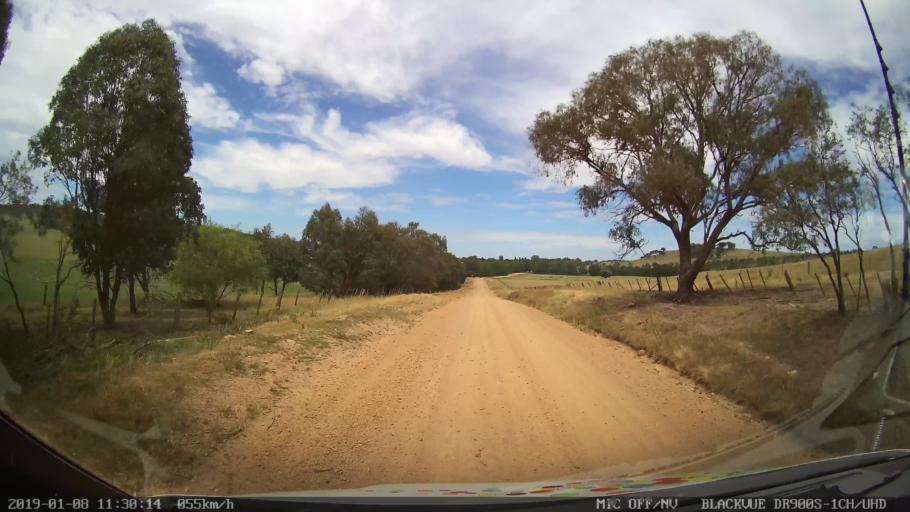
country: AU
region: New South Wales
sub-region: Guyra
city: Guyra
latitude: -30.3065
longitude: 151.5454
